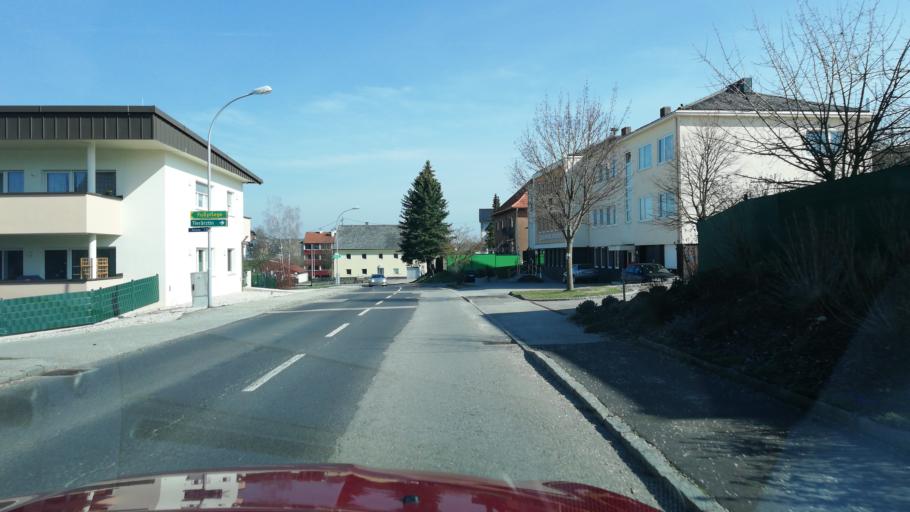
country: AT
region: Upper Austria
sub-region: Politischer Bezirk Kirchdorf an der Krems
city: Kremsmunster
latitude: 48.0959
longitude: 14.1112
